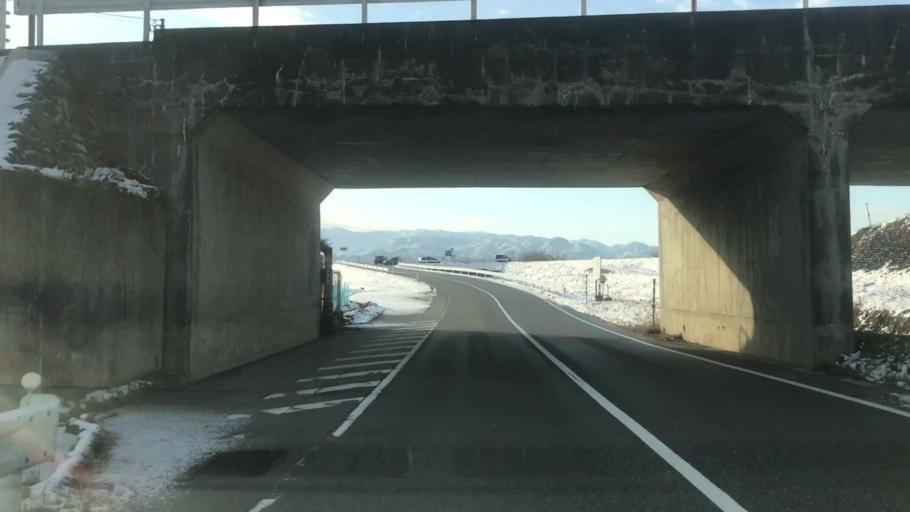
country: JP
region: Toyama
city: Toyama-shi
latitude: 36.6489
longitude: 137.2863
